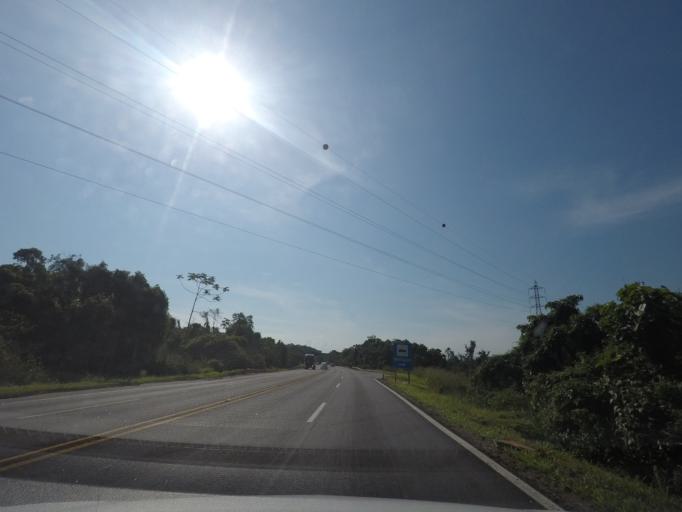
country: BR
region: Parana
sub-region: Paranagua
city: Paranagua
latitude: -25.5746
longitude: -48.6129
